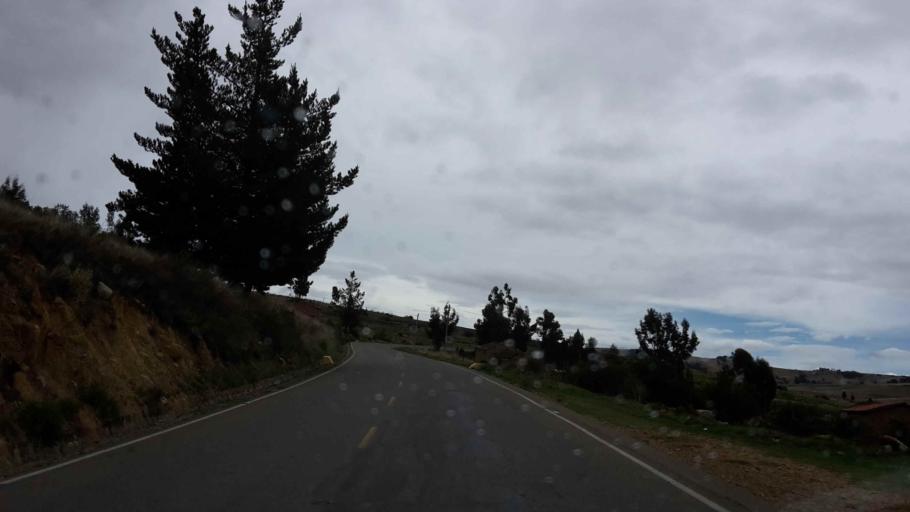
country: BO
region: Cochabamba
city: Arani
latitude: -17.4603
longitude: -65.6754
